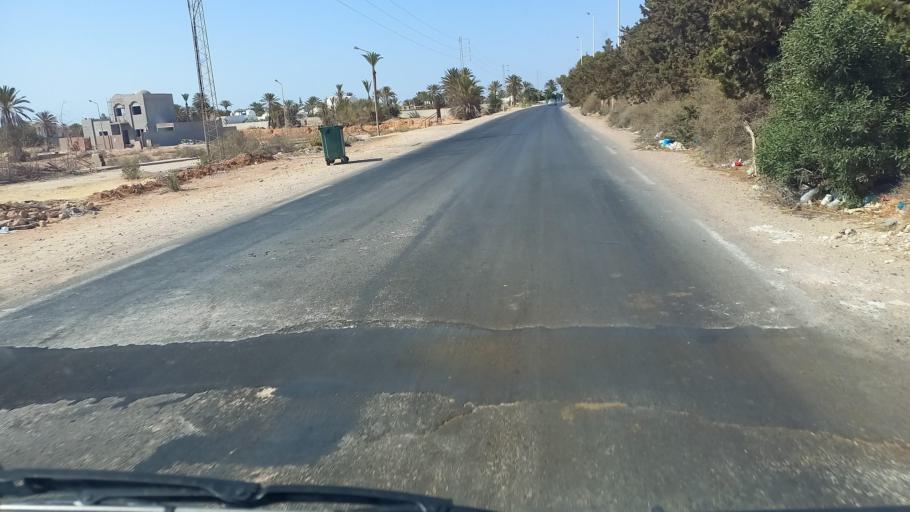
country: TN
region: Madanin
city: Midoun
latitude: 33.7727
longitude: 11.0267
